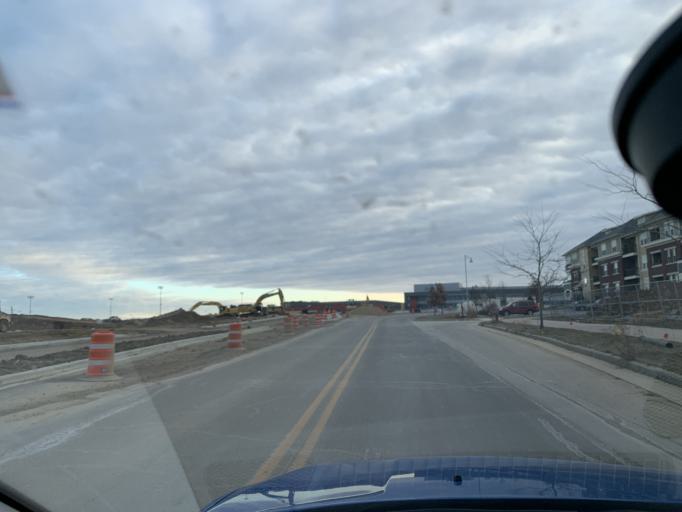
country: US
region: Wisconsin
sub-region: Dane County
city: Verona
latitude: 42.9873
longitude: -89.5532
